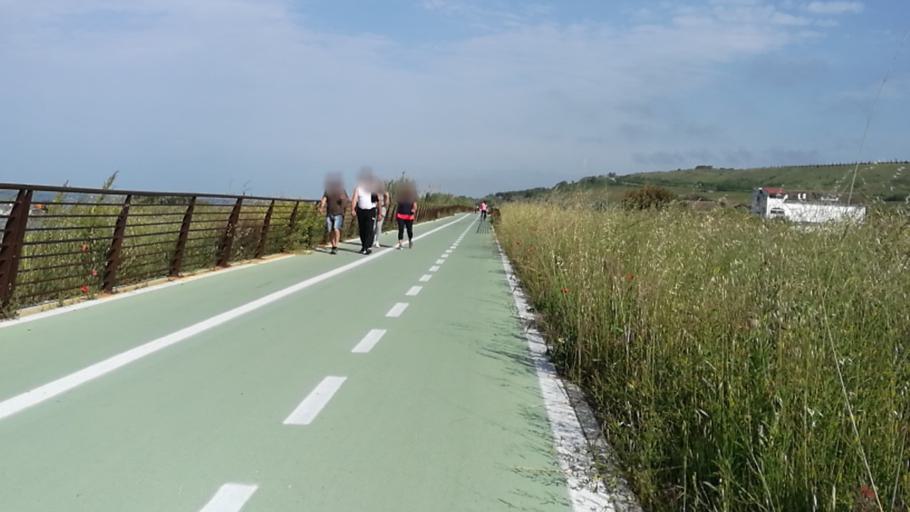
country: IT
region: Abruzzo
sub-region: Provincia di Chieti
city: Casalbordino-Miracoli
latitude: 42.2043
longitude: 14.6040
